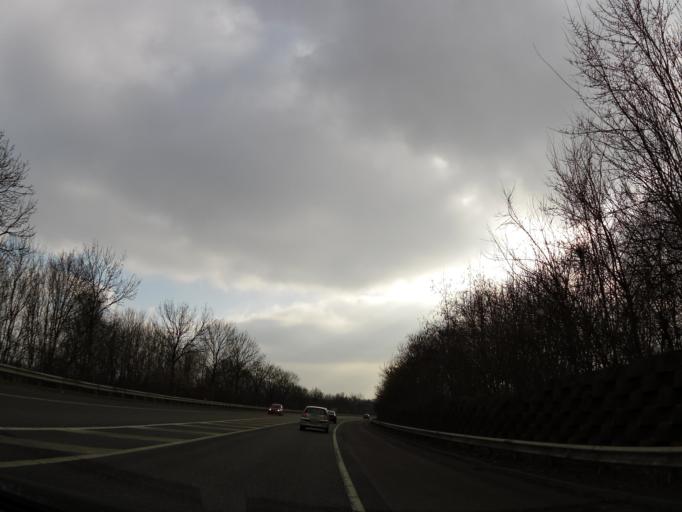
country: NL
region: Limburg
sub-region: Gemeente Kerkrade
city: Kerkrade
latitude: 50.9034
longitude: 6.0458
